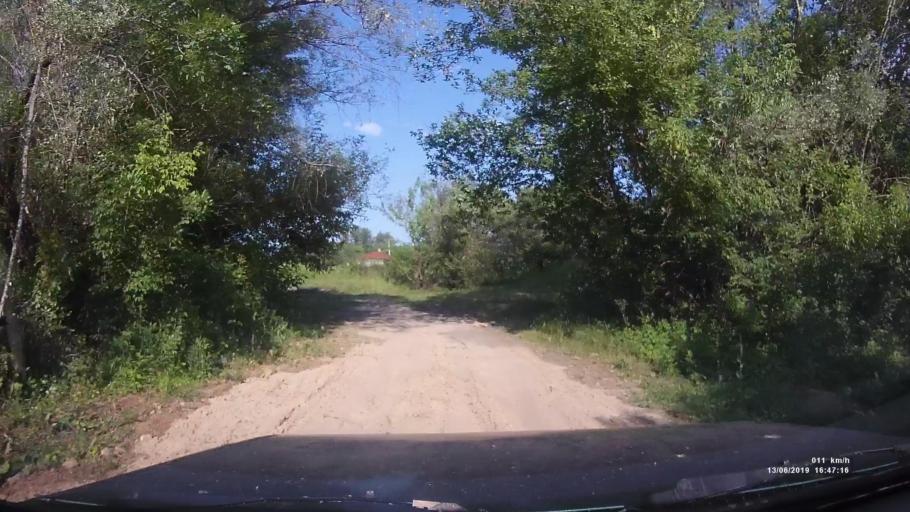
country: RU
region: Rostov
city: Kazanskaya
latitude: 49.9442
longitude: 41.4309
